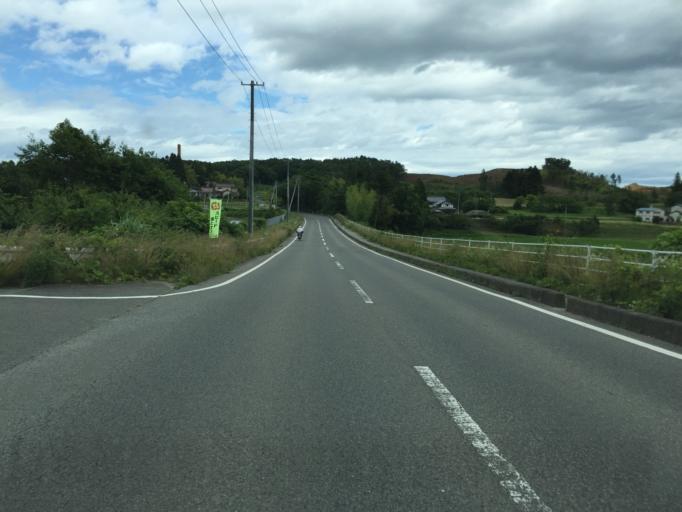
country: JP
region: Fukushima
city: Namie
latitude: 37.6615
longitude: 140.9618
